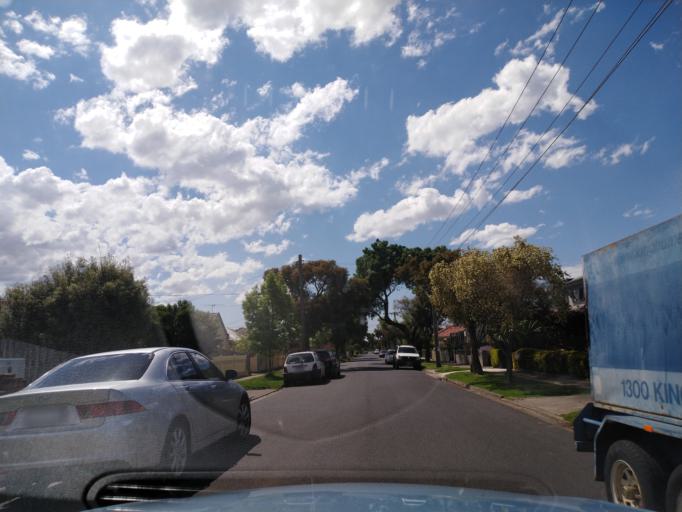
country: AU
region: Victoria
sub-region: Hobsons Bay
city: South Kingsville
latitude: -37.8326
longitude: 144.8703
